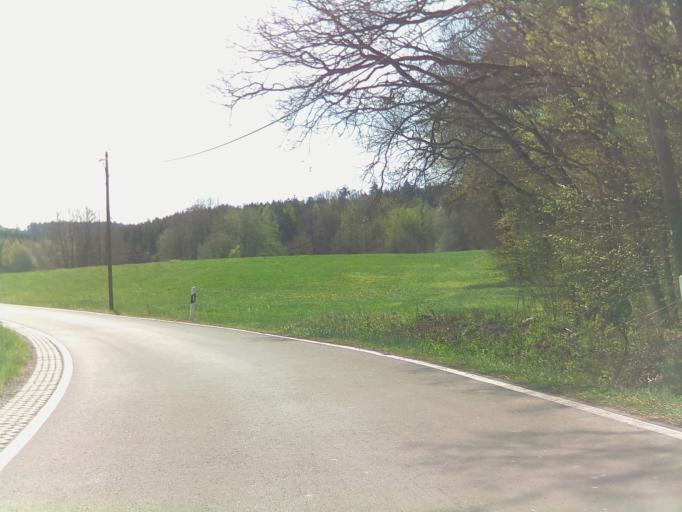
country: DE
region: Thuringia
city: Hellingen
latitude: 50.2516
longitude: 10.6617
